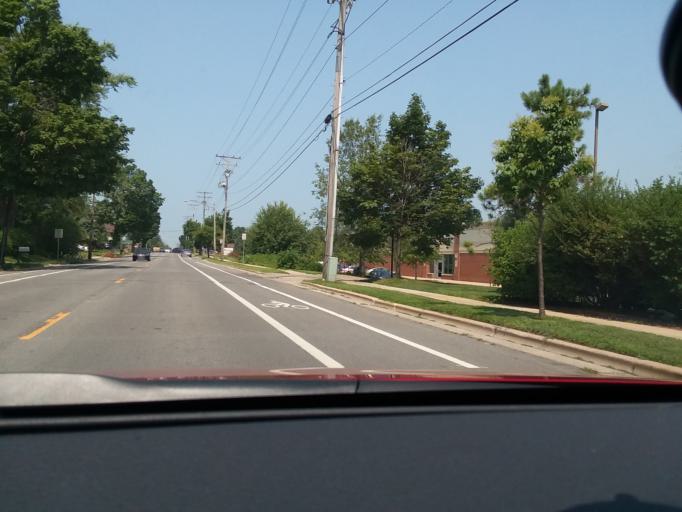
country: US
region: Wisconsin
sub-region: Dane County
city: Monona
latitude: 43.1168
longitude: -89.3187
